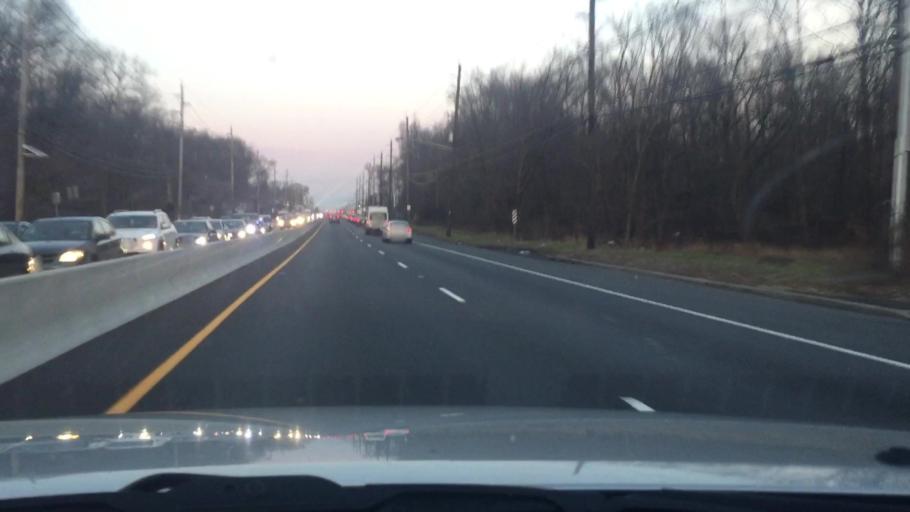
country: US
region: New Jersey
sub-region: Middlesex County
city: Kendall Park
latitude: 40.4323
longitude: -74.5146
